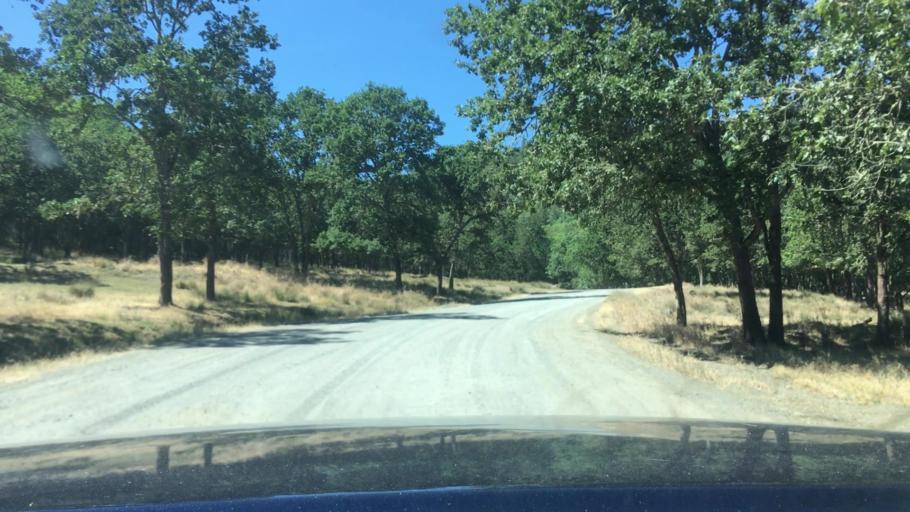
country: US
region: Oregon
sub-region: Douglas County
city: Winston
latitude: 43.1371
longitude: -123.4405
